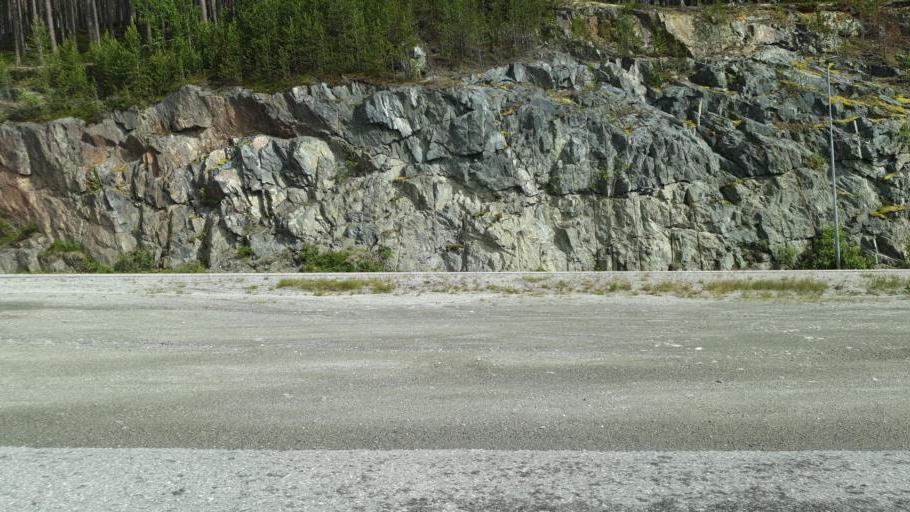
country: NO
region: Oppland
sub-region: Dovre
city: Dombas
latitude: 62.0821
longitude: 9.1382
